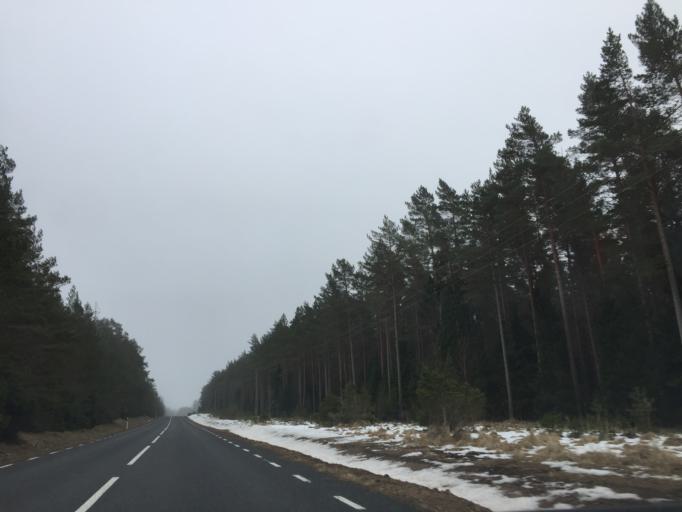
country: EE
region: Saare
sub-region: Kuressaare linn
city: Kuressaare
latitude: 58.4690
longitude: 22.0346
